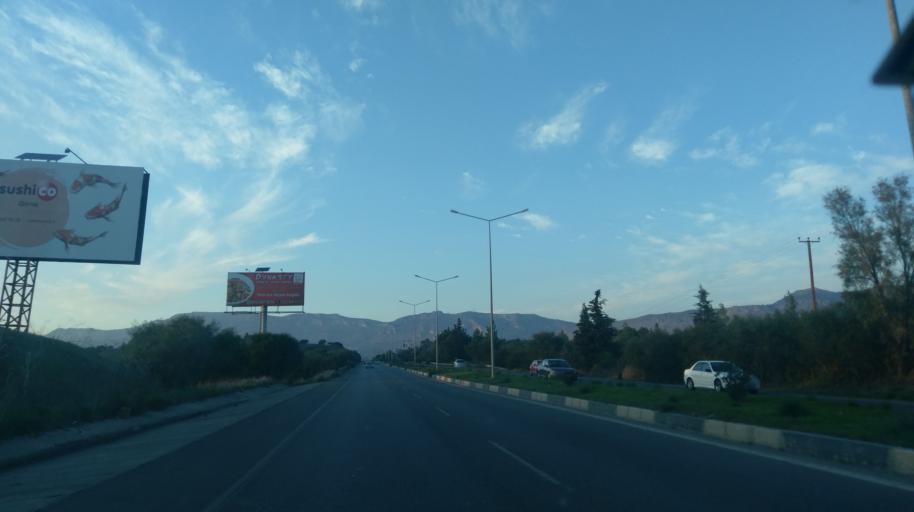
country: CY
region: Lefkosia
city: Nicosia
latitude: 35.2457
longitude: 33.3068
